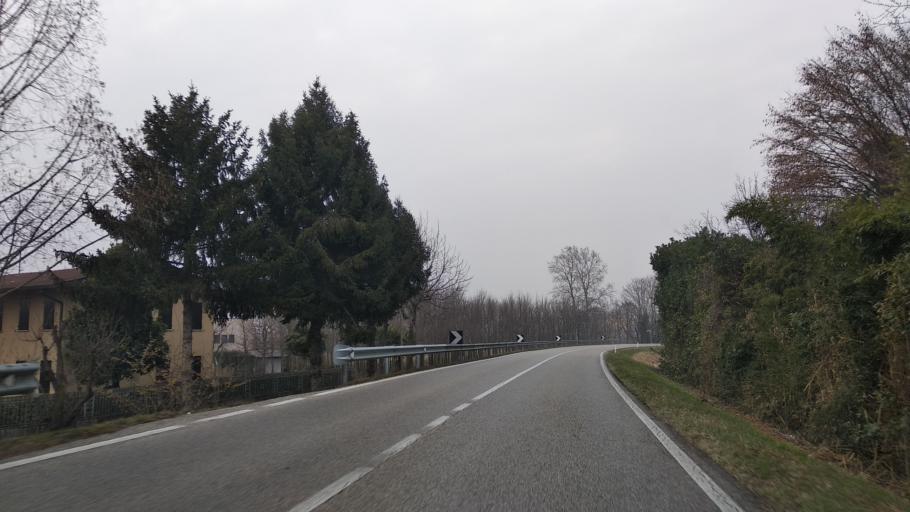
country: IT
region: Veneto
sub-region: Provincia di Padova
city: Tavo
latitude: 45.5094
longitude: 11.8615
